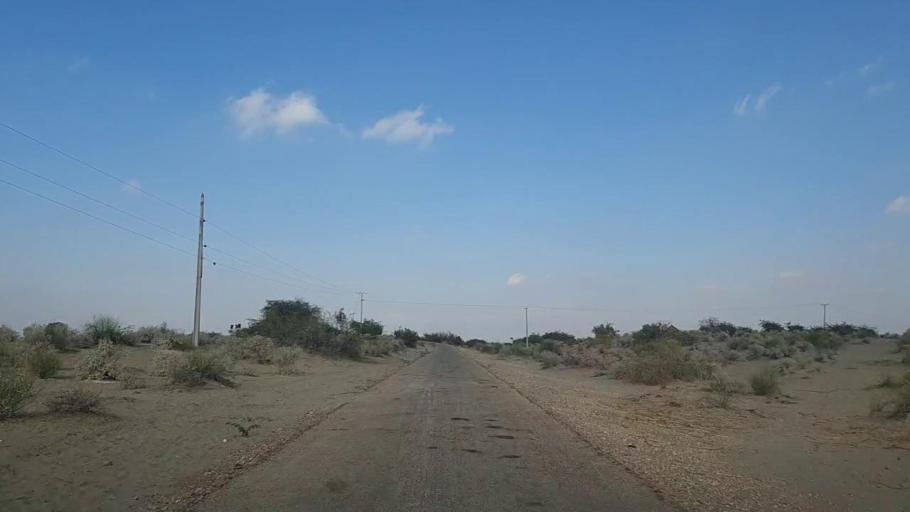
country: PK
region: Sindh
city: Tando Mittha Khan
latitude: 26.0042
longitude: 69.2479
